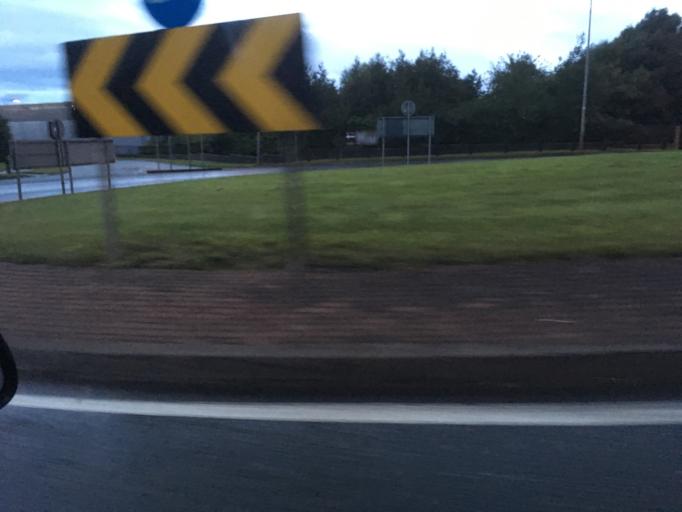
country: IE
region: Leinster
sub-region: Kildare
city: Naas
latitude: 53.2132
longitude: -6.7066
